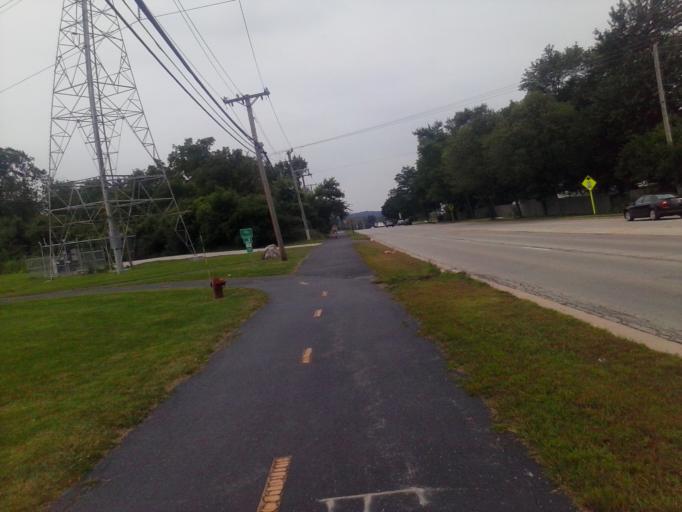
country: US
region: Illinois
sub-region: DuPage County
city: Woodridge
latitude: 41.7631
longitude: -88.0595
